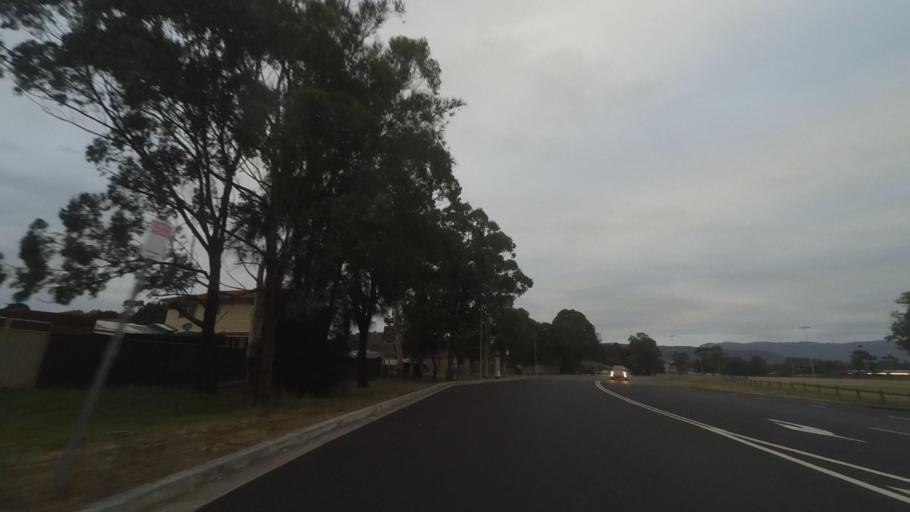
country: AU
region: New South Wales
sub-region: Shellharbour
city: Albion Park Rail
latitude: -34.5690
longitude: 150.8060
